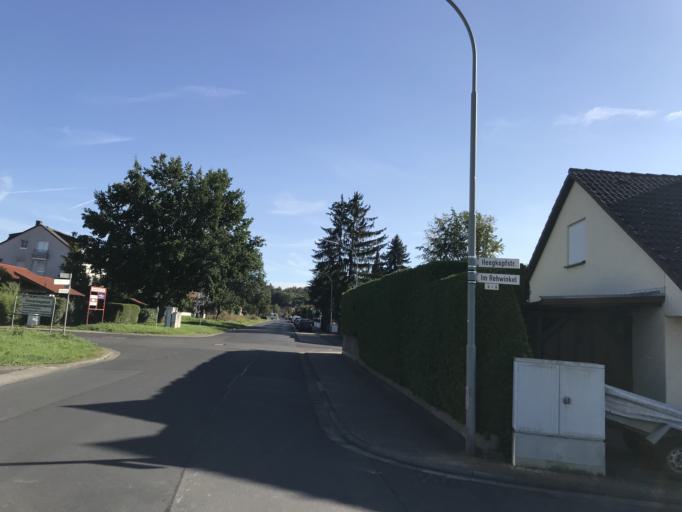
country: DE
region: Hesse
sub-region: Regierungsbezirk Darmstadt
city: Altenstadt
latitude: 50.2728
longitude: 8.9630
